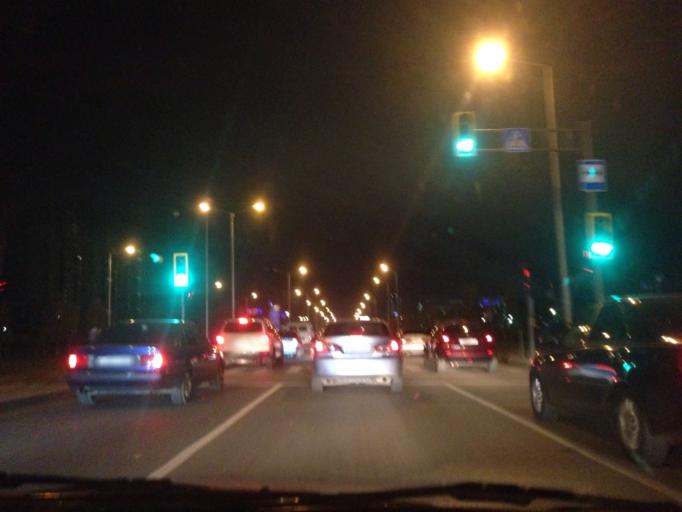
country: KZ
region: Astana Qalasy
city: Astana
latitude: 51.1141
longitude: 71.4001
